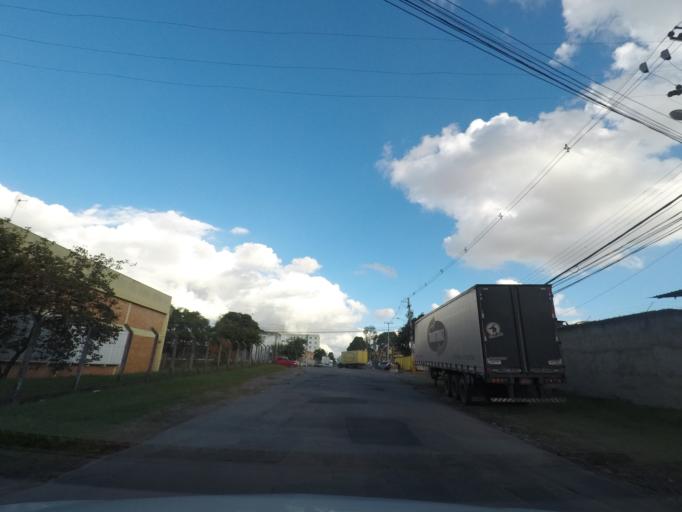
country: BR
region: Parana
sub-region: Curitiba
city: Curitiba
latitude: -25.4812
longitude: -49.2628
